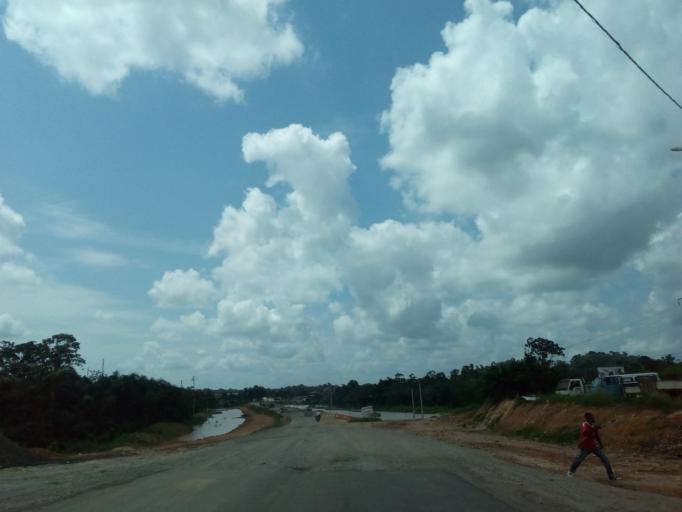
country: CI
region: Sud-Comoe
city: Mafere
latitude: 5.2834
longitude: -2.7969
